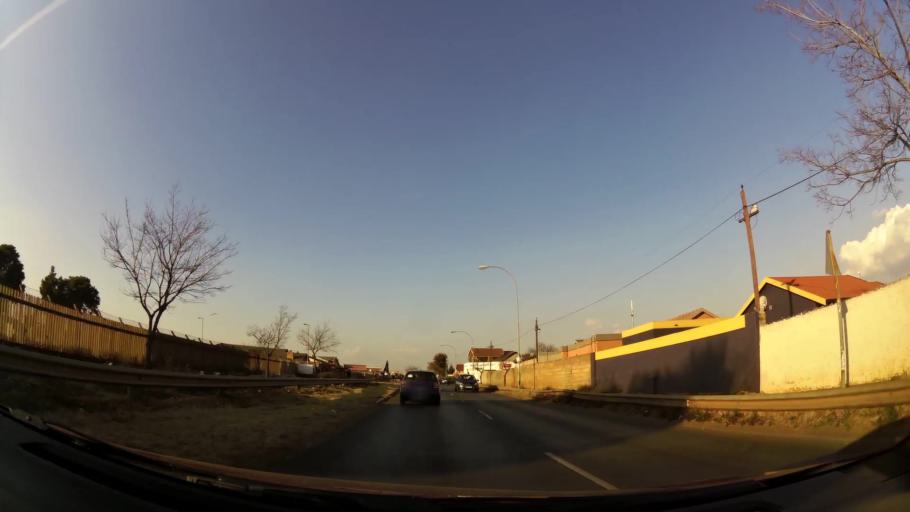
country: ZA
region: Gauteng
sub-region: City of Johannesburg Metropolitan Municipality
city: Soweto
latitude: -26.2301
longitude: 27.8471
